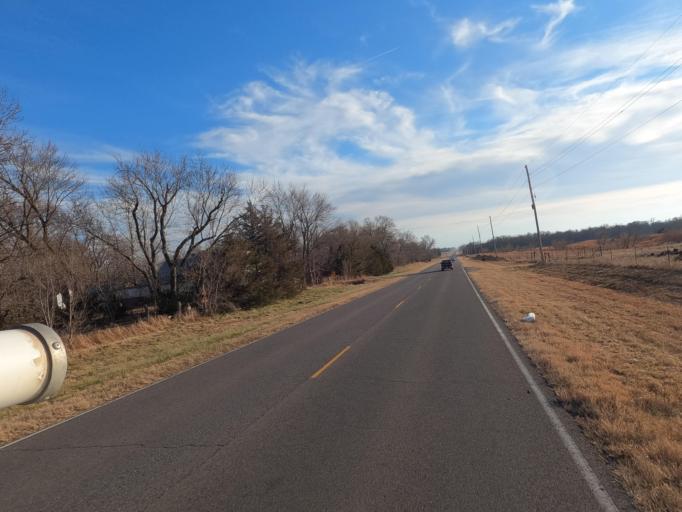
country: US
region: Kansas
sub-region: Reno County
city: Buhler
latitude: 38.0477
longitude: -97.7753
